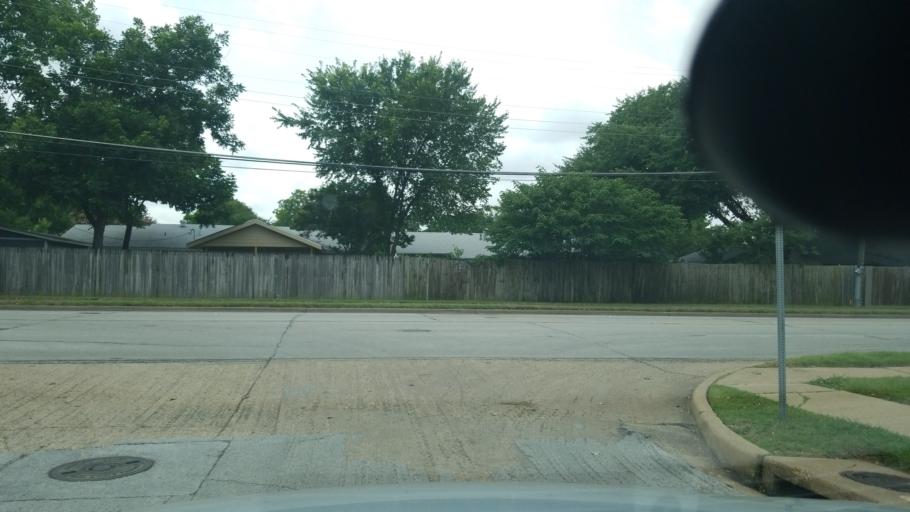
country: US
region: Texas
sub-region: Dallas County
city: Irving
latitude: 32.8444
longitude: -96.9620
